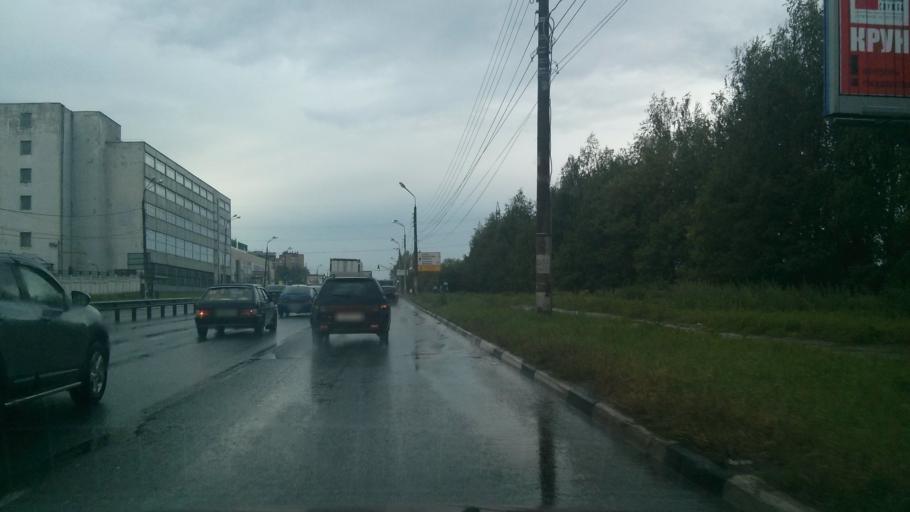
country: RU
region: Nizjnij Novgorod
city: Nizhniy Novgorod
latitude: 56.2414
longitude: 43.9829
